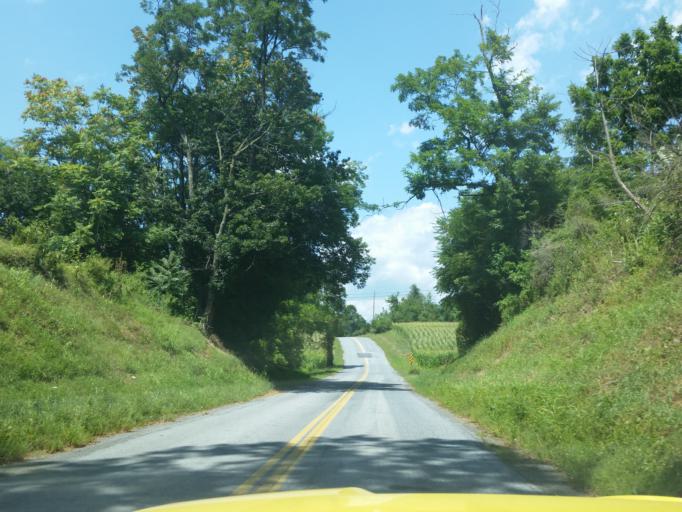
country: US
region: Pennsylvania
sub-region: Lebanon County
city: Palmyra
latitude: 40.3988
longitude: -76.6030
